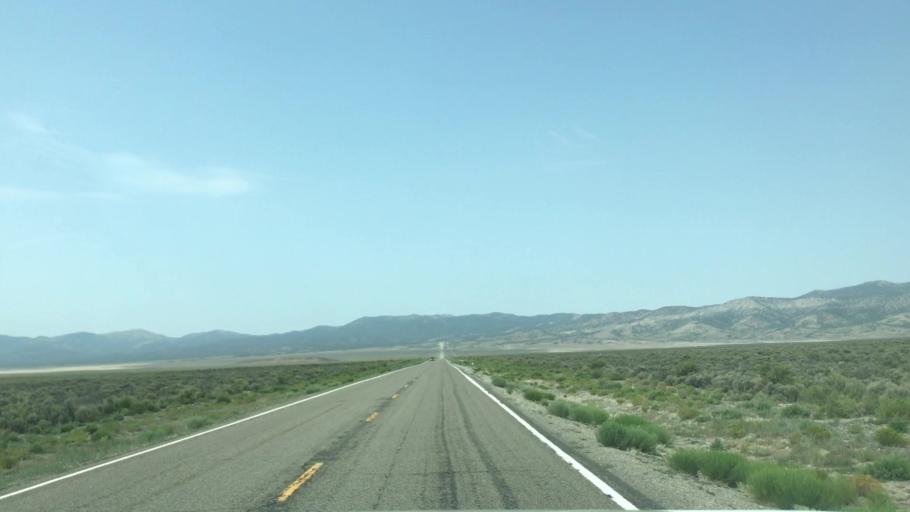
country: US
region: Nevada
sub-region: White Pine County
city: Ely
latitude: 39.0572
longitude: -114.4874
